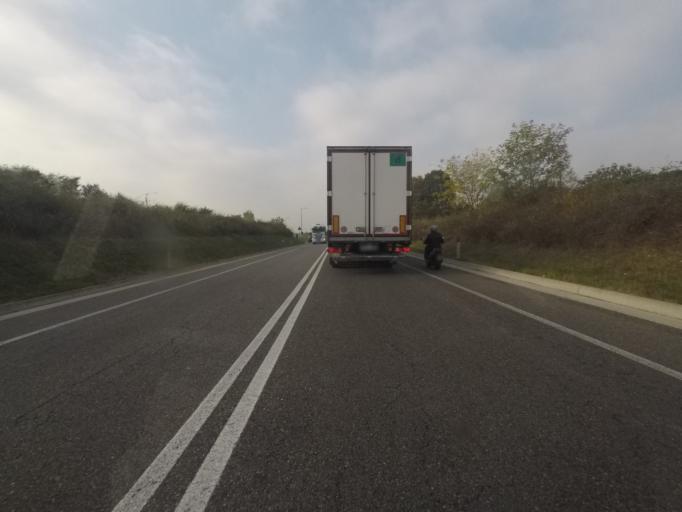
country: IT
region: Lombardy
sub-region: Provincia di Monza e Brianza
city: Burago di Molgora
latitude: 45.6097
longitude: 9.3849
